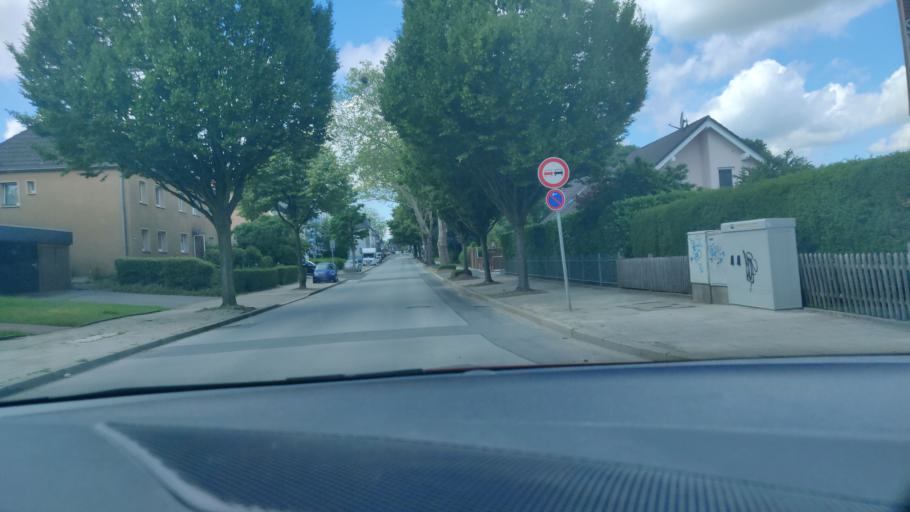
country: DE
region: North Rhine-Westphalia
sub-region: Regierungsbezirk Dusseldorf
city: Heiligenhaus
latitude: 51.3318
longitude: 6.9761
